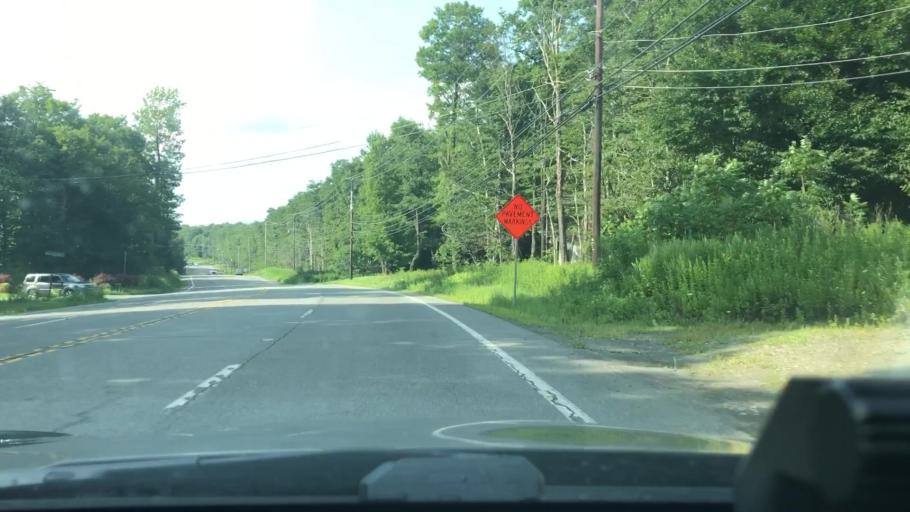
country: US
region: Pennsylvania
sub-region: Lackawanna County
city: Moscow
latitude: 41.2746
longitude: -75.5062
